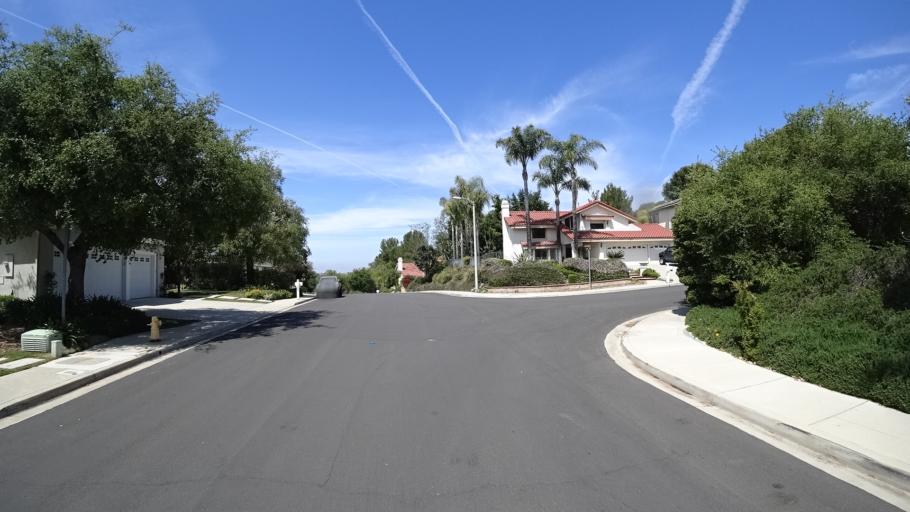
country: US
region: California
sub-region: Ventura County
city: Thousand Oaks
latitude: 34.1967
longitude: -118.8453
